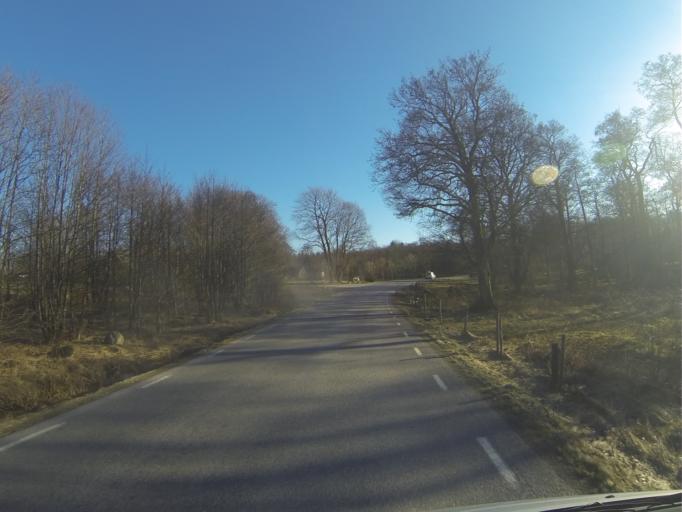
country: SE
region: Skane
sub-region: Horby Kommun
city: Hoerby
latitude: 55.8907
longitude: 13.6669
